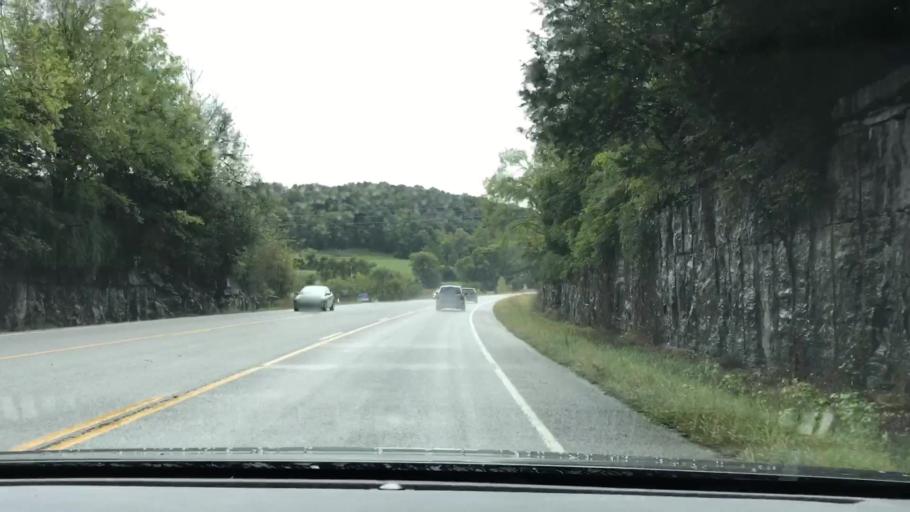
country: US
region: Tennessee
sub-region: Smith County
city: South Carthage
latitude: 36.2052
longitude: -85.9519
